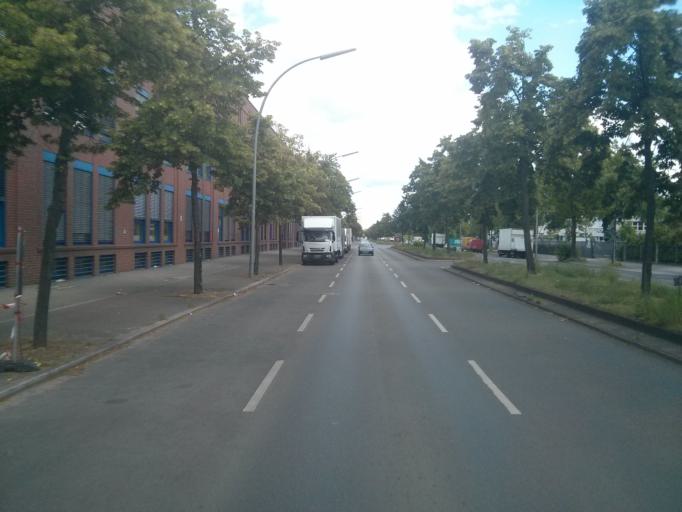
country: DE
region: Berlin
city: Wilhelmstadt
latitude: 52.5337
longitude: 13.1724
